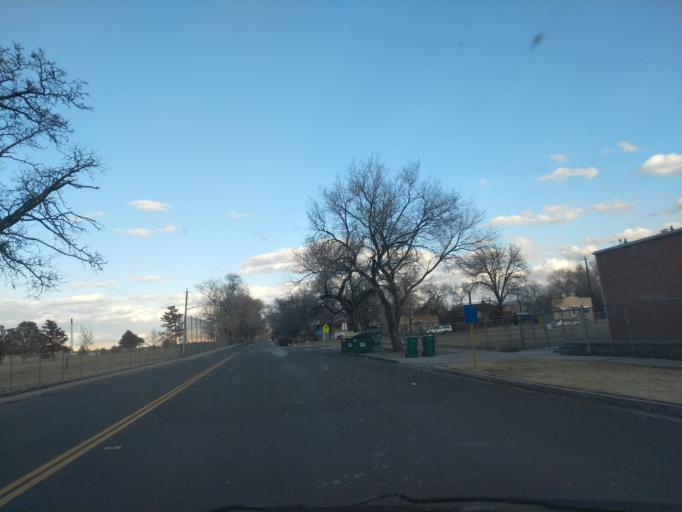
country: US
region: Colorado
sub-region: Mesa County
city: Grand Junction
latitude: 39.0734
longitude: -108.5487
